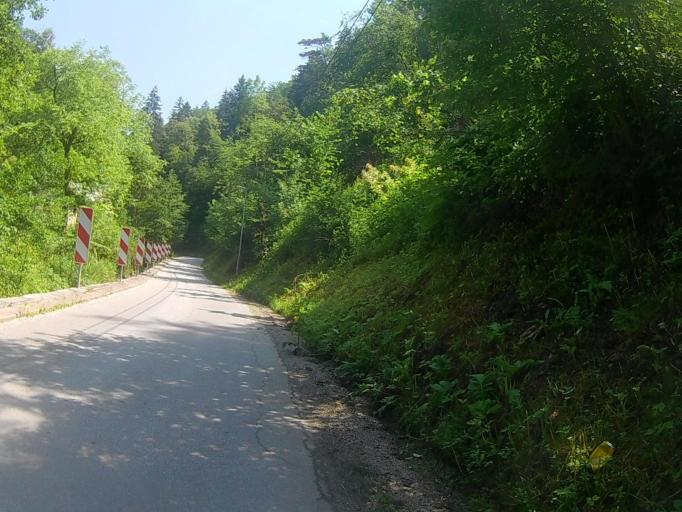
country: SI
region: Maribor
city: Bresternica
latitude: 46.5711
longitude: 15.5759
